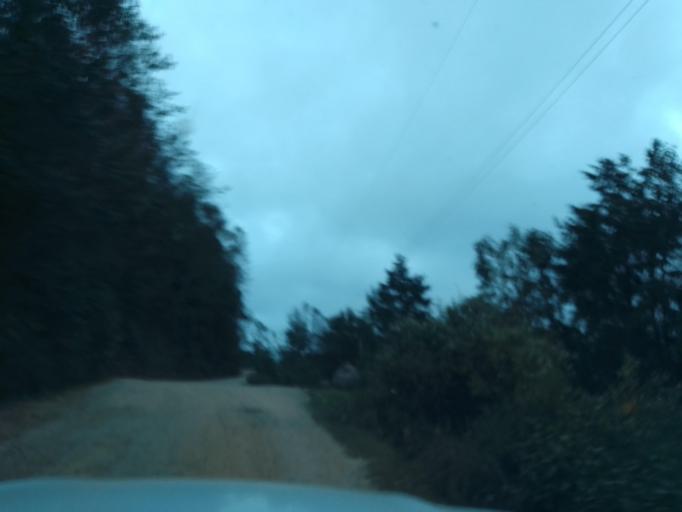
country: MX
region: Chiapas
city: Motozintla de Mendoza
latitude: 15.2201
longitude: -92.2361
